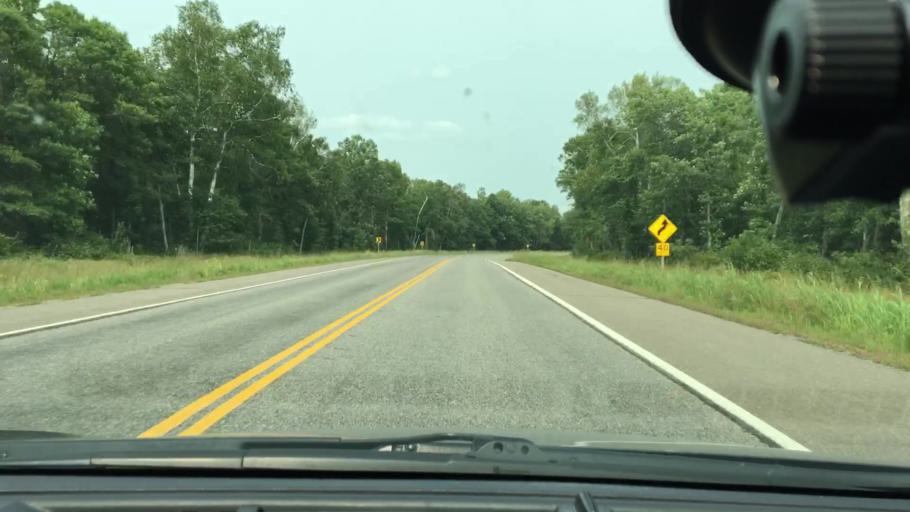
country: US
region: Minnesota
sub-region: Crow Wing County
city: Cross Lake
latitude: 46.6985
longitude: -94.0658
